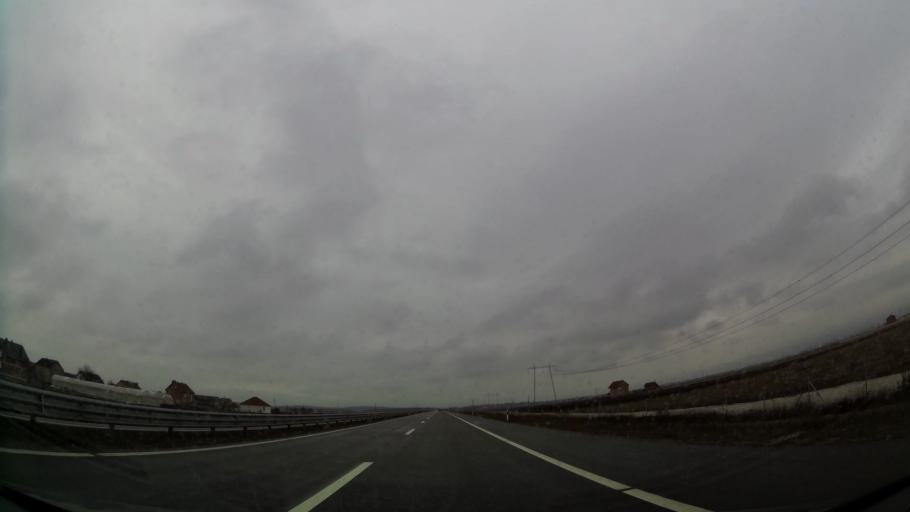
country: XK
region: Ferizaj
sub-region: Komuna e Ferizajt
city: Ferizaj
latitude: 42.3968
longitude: 21.1990
